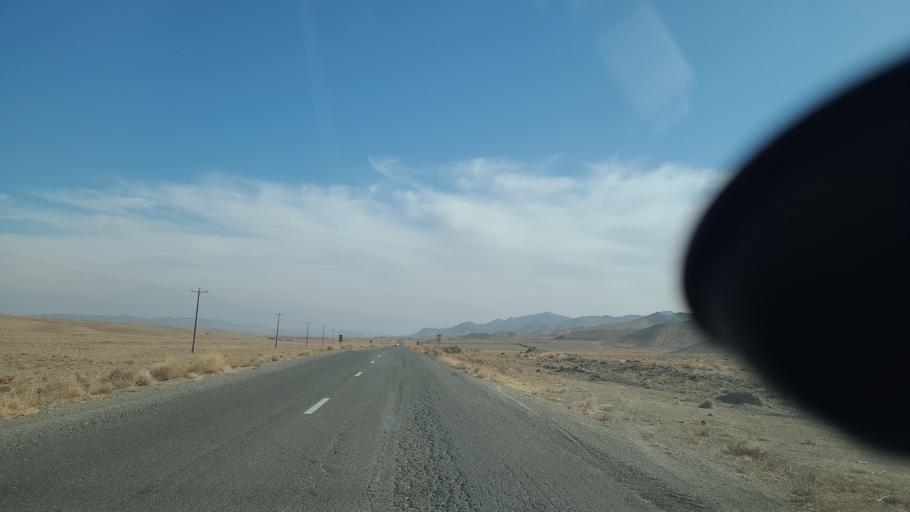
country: IR
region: Razavi Khorasan
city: Fariman
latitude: 35.5883
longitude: 59.6311
